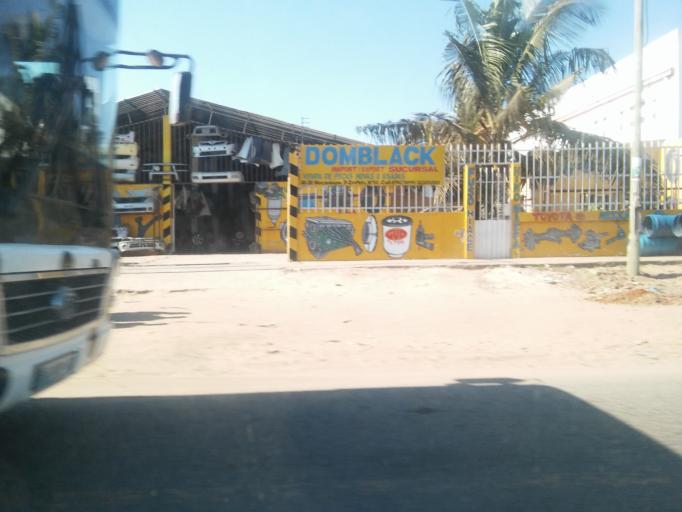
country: MZ
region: Maputo City
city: Maputo
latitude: -25.8601
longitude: 32.5668
